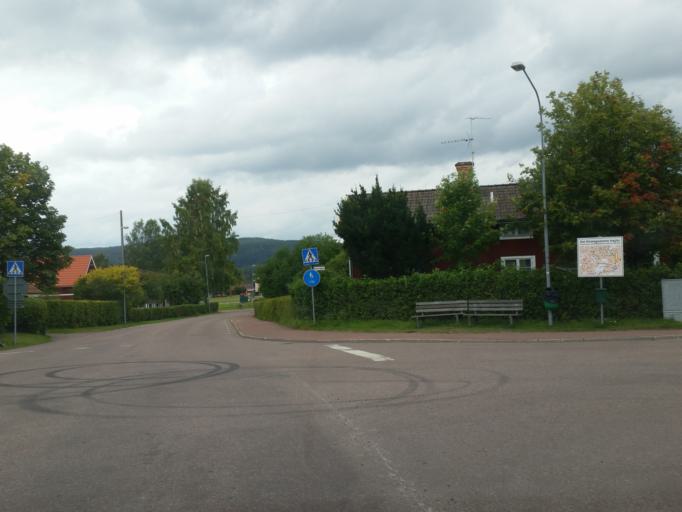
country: SE
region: Dalarna
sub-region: Leksand Municipality
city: Smedby
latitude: 60.6798
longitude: 15.0969
